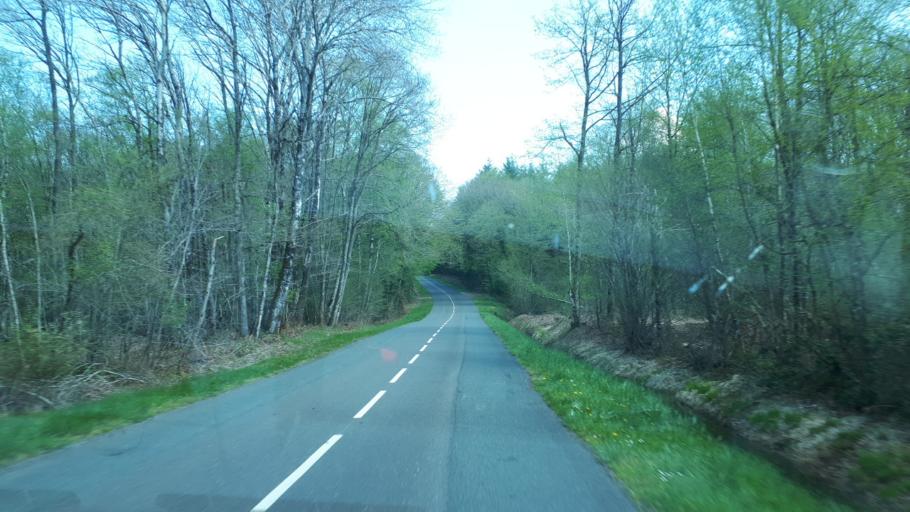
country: FR
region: Centre
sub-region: Departement du Cher
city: Henrichemont
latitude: 47.2945
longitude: 2.6077
